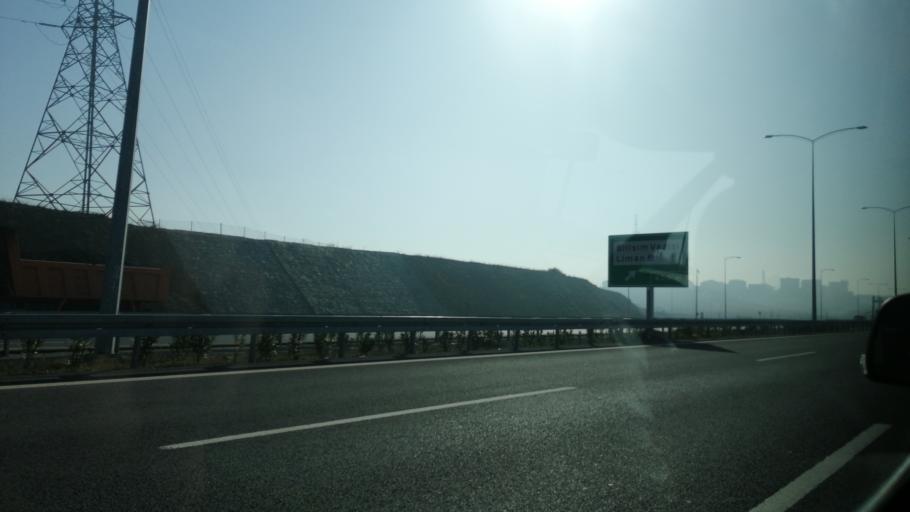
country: TR
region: Kocaeli
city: Tavsanli
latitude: 40.7878
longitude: 29.5146
